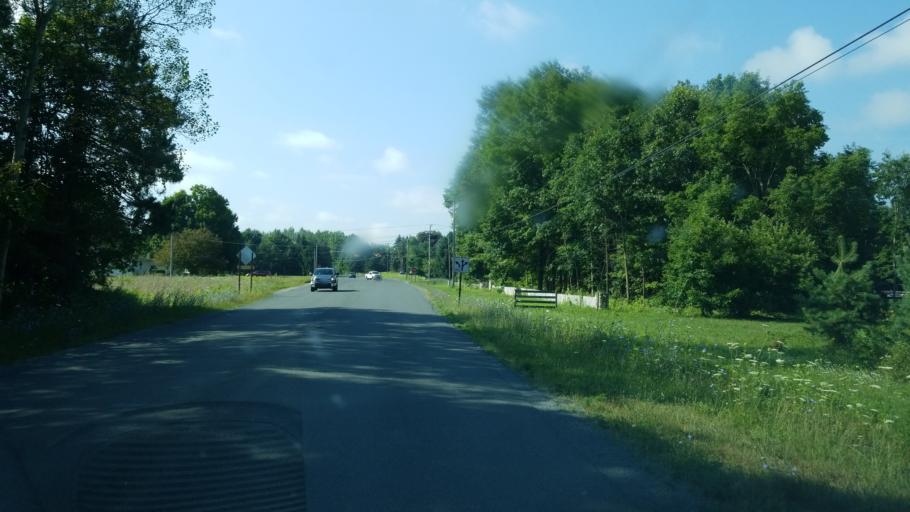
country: US
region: Michigan
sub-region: Kent County
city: Sparta
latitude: 43.1180
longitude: -85.6508
